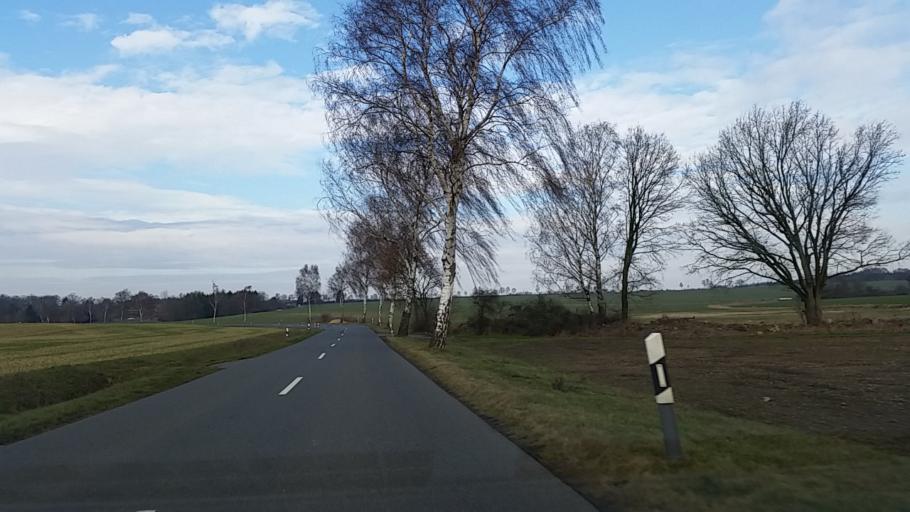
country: DE
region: Lower Saxony
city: Romstedt
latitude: 53.1126
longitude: 10.6477
